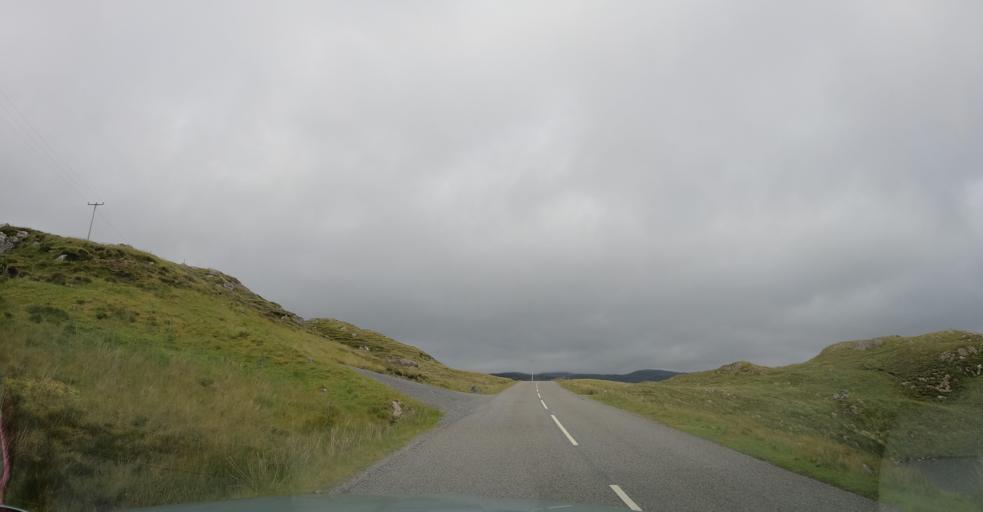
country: GB
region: Scotland
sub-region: Eilean Siar
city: Harris
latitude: 57.8919
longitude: -6.8019
